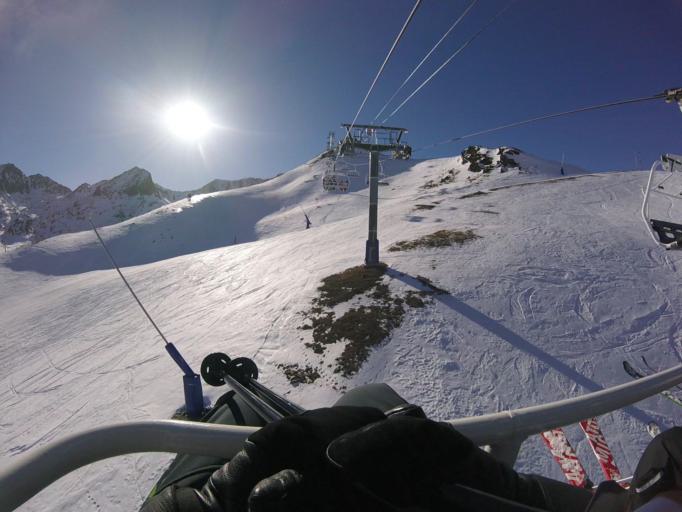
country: AD
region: Encamp
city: Pas de la Casa
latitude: 42.5347
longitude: 1.7298
